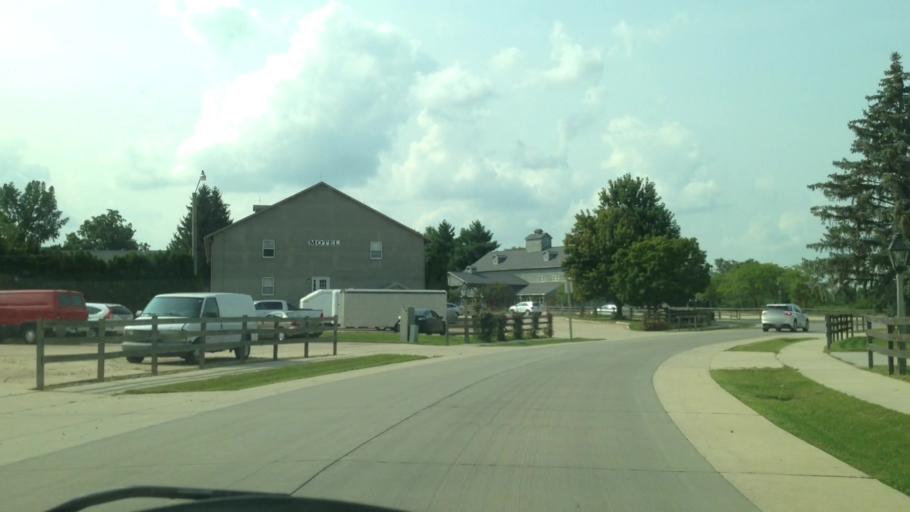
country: US
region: Iowa
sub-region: Benton County
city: Walford
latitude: 41.7986
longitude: -91.8660
